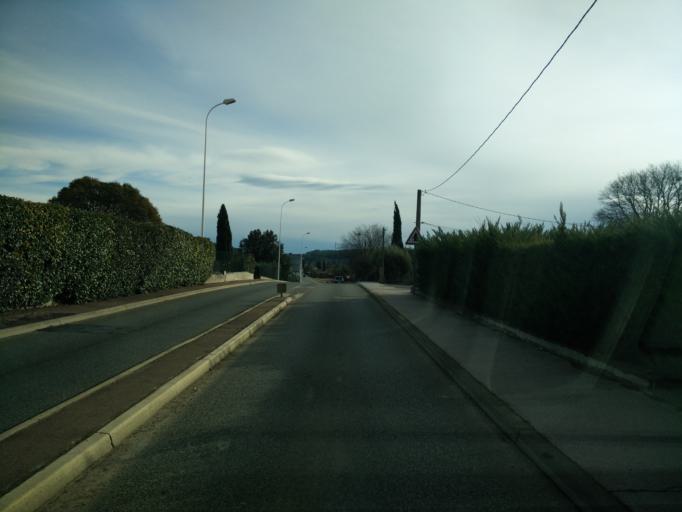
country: FR
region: Provence-Alpes-Cote d'Azur
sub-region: Departement du Var
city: Lorgues
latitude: 43.4872
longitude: 6.3657
